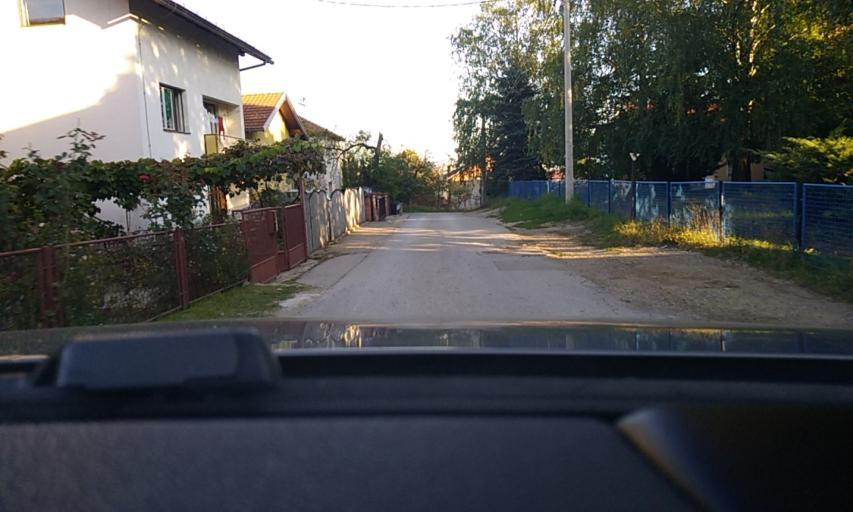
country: BA
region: Republika Srpska
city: Banja Luka
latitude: 44.7824
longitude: 17.1878
